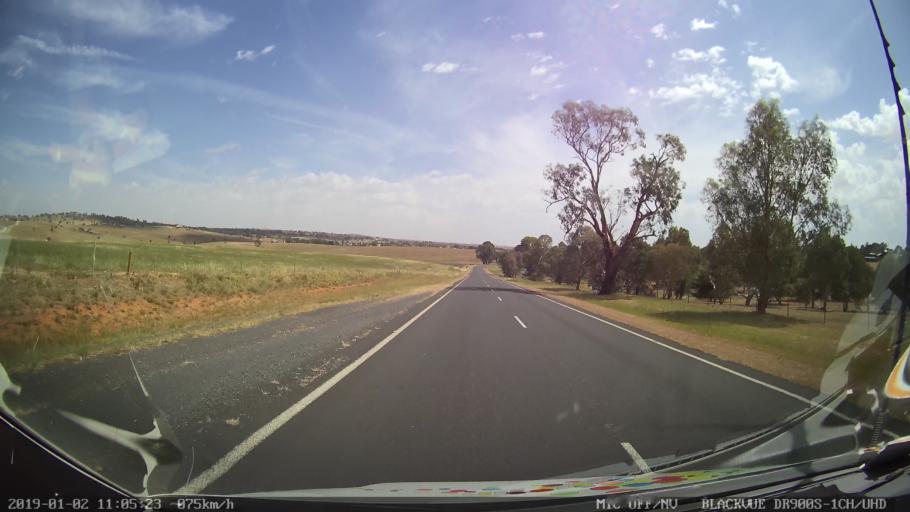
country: AU
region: New South Wales
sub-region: Young
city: Young
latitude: -34.5655
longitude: 148.3540
